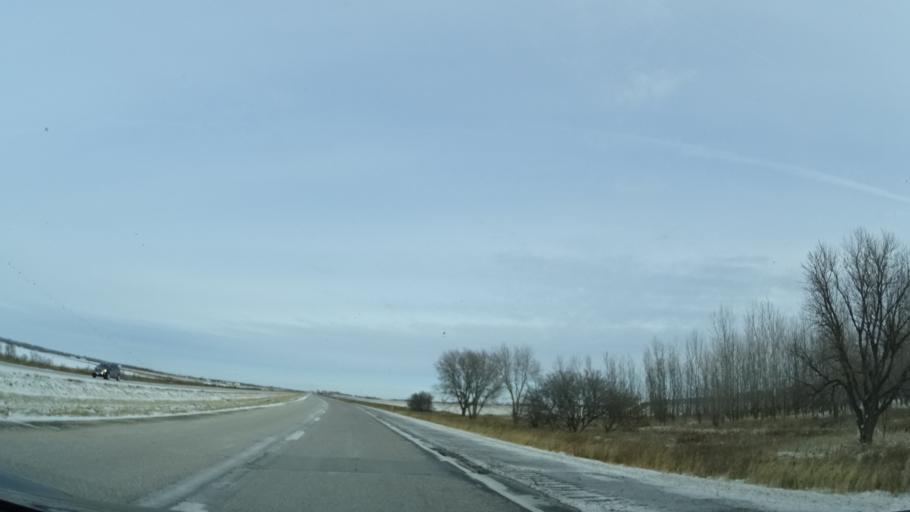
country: US
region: Nebraska
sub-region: Burt County
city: Tekamah
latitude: 41.7603
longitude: -96.0455
